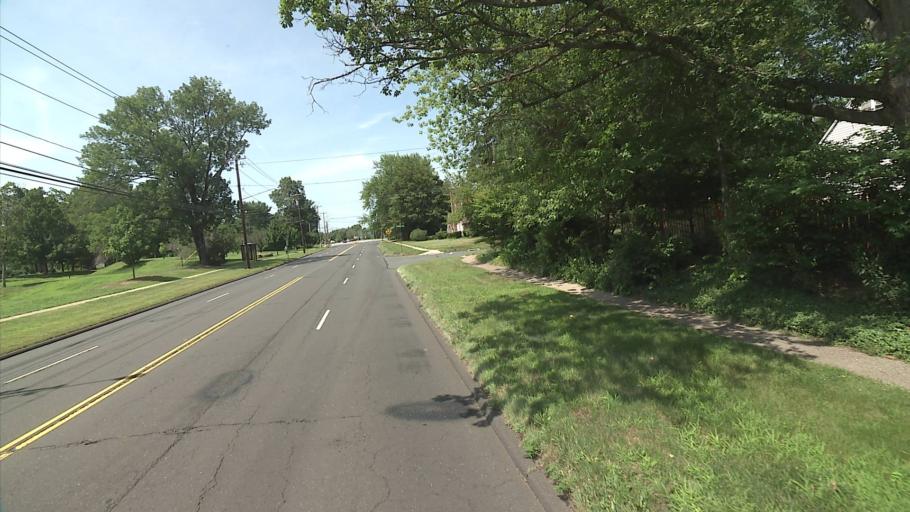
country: US
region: Connecticut
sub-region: Hartford County
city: West Hartford
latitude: 41.7303
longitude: -72.7500
